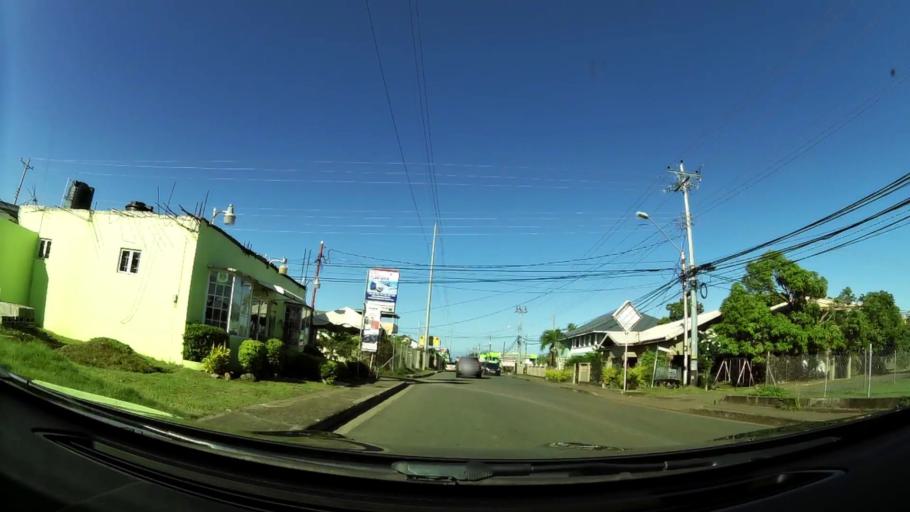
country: TT
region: Tobago
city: Scarborough
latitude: 11.1536
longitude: -60.8354
